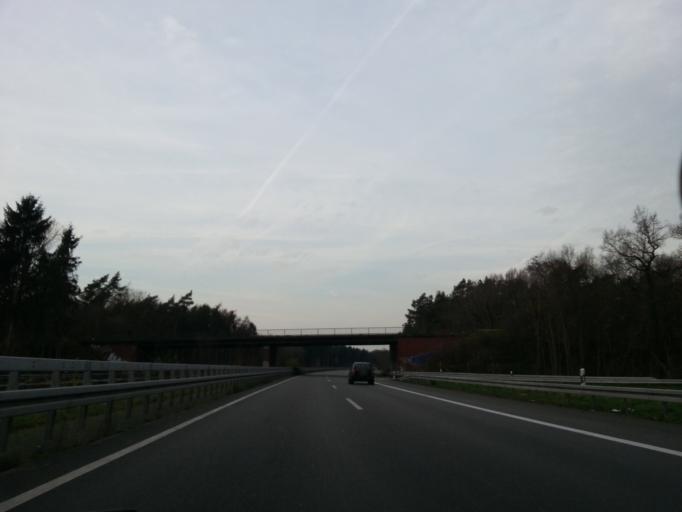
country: DE
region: North Rhine-Westphalia
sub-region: Regierungsbezirk Dusseldorf
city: Mehrhoog
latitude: 51.7819
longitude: 6.5066
